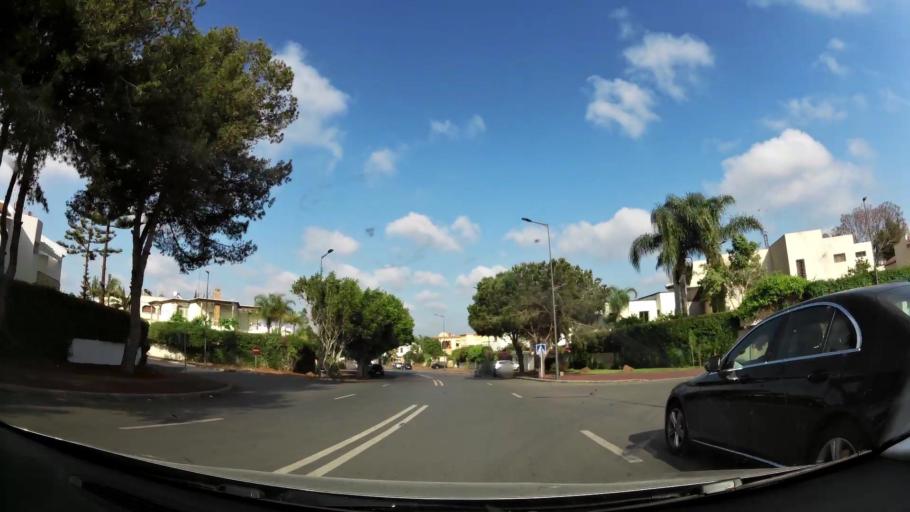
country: MA
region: Rabat-Sale-Zemmour-Zaer
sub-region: Skhirate-Temara
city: Temara
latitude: 33.9495
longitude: -6.8669
